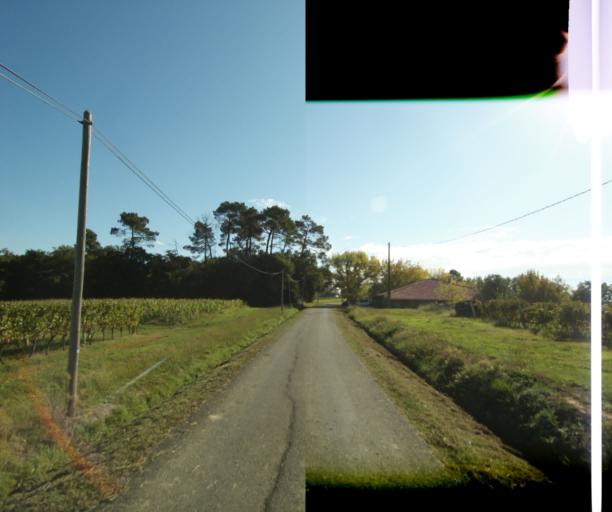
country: FR
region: Aquitaine
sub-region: Departement des Landes
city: Gabarret
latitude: 43.9066
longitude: 0.0147
